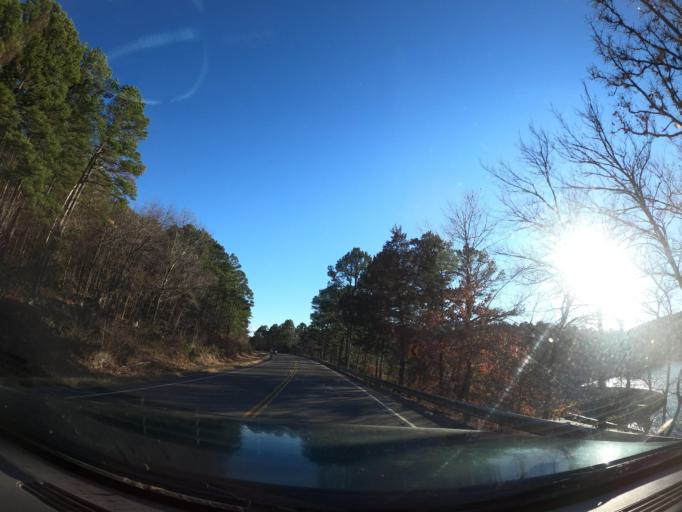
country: US
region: Oklahoma
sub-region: Latimer County
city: Wilburton
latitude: 34.9777
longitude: -95.3594
